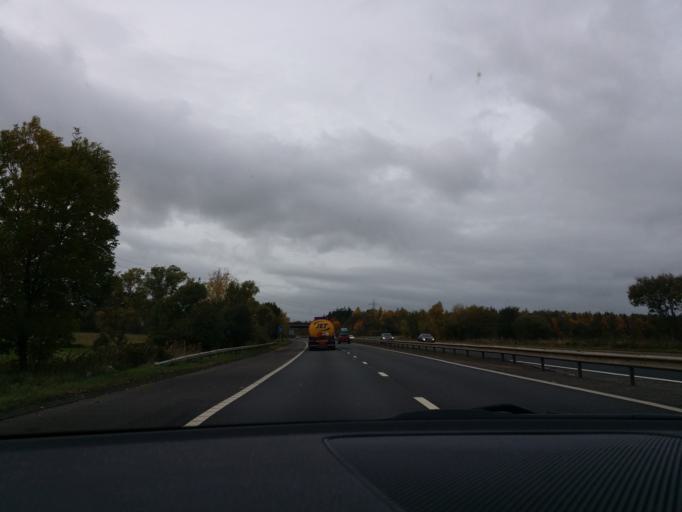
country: GB
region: Scotland
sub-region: Falkirk
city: Airth
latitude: 56.0416
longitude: -3.7782
